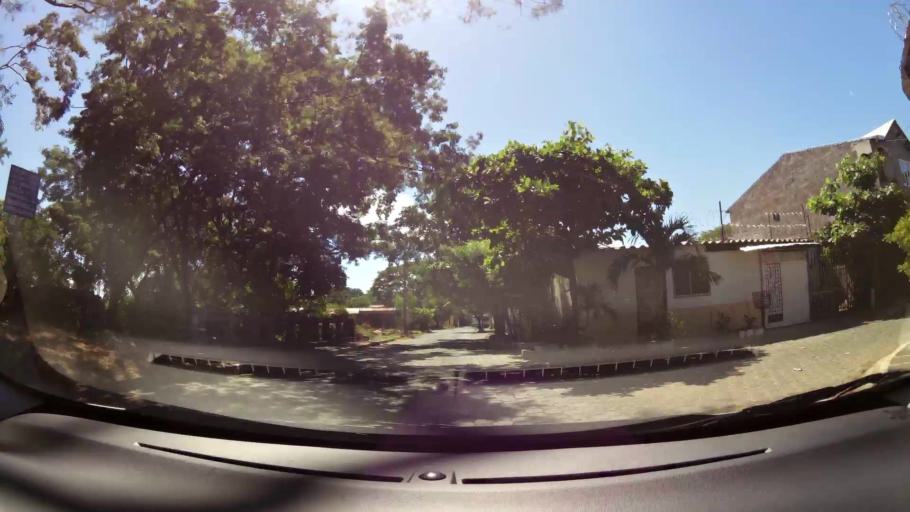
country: SV
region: San Miguel
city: San Miguel
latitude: 13.4807
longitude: -88.1652
